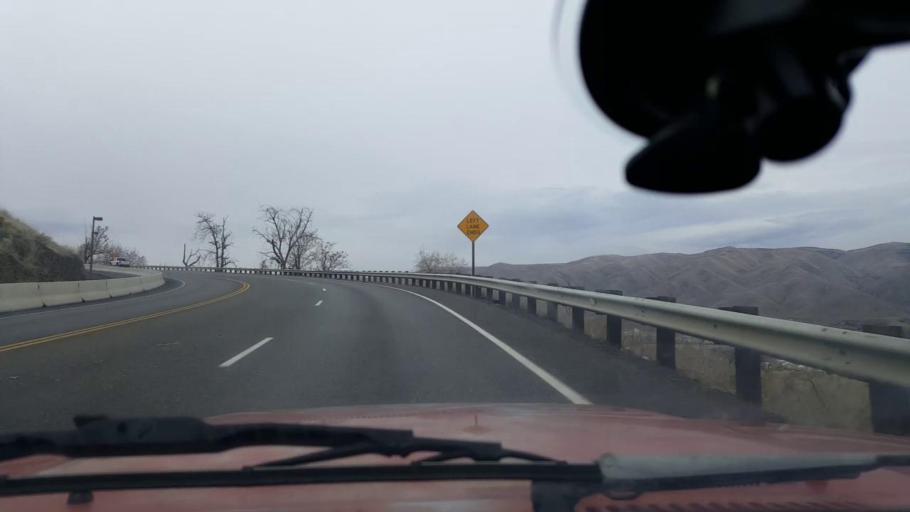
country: US
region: Washington
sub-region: Asotin County
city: West Clarkston-Highland
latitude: 46.4010
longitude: -117.0739
